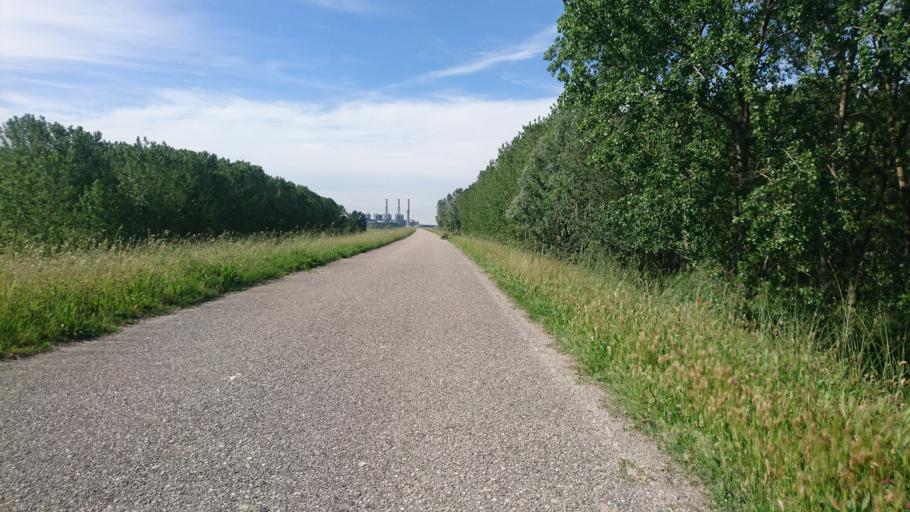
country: IT
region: Veneto
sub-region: Provincia di Rovigo
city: Bergantino
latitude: 45.0485
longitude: 11.2545
